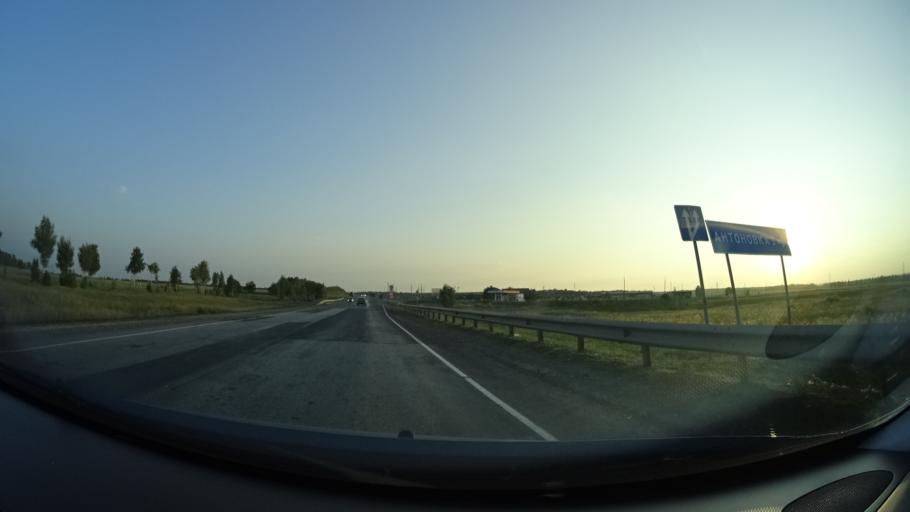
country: RU
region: Samara
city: Sernovodsk
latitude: 53.9333
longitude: 51.3353
